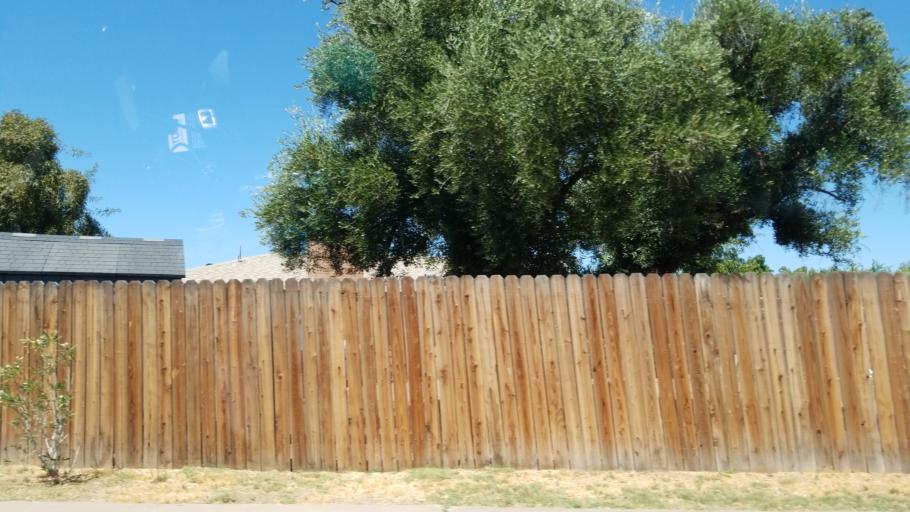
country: US
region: Arizona
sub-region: Maricopa County
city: Phoenix
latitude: 33.5200
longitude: -112.0869
